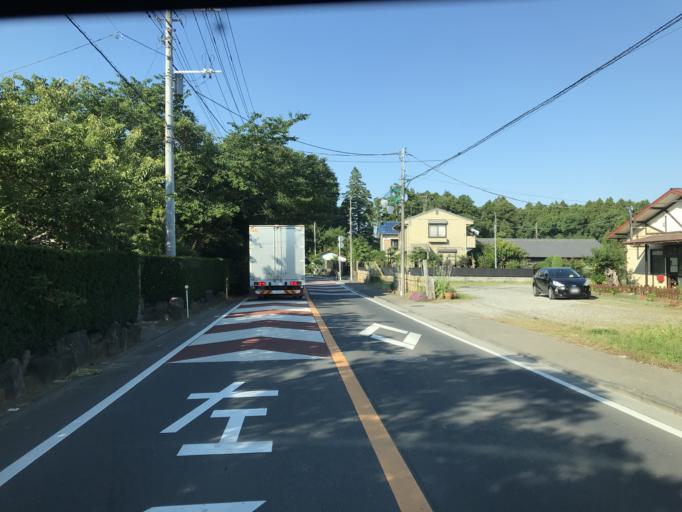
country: JP
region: Chiba
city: Chiba
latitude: 35.5621
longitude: 140.2014
